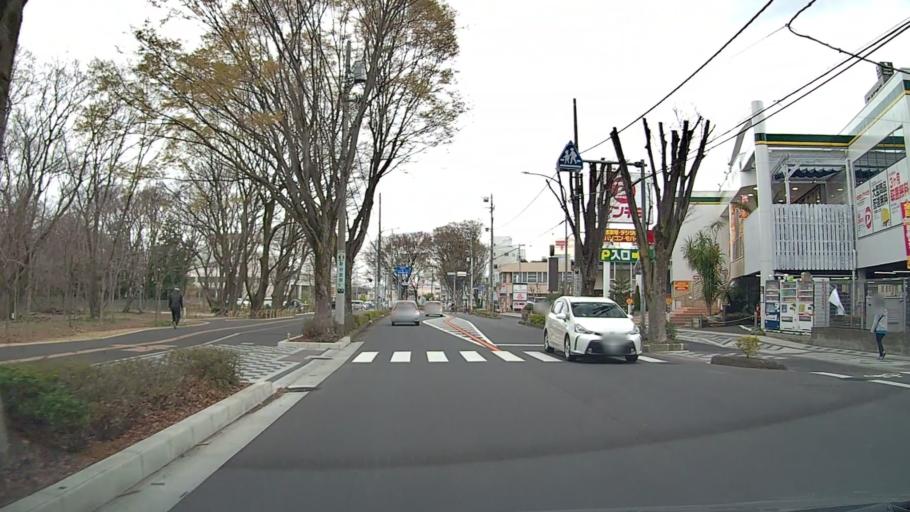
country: JP
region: Saitama
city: Asaka
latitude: 35.7949
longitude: 139.5947
